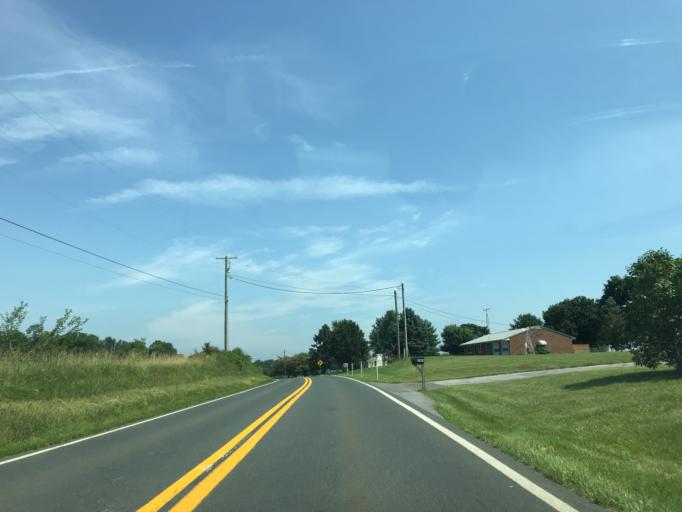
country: US
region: Maryland
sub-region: Carroll County
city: Taneytown
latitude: 39.6300
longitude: -77.1493
